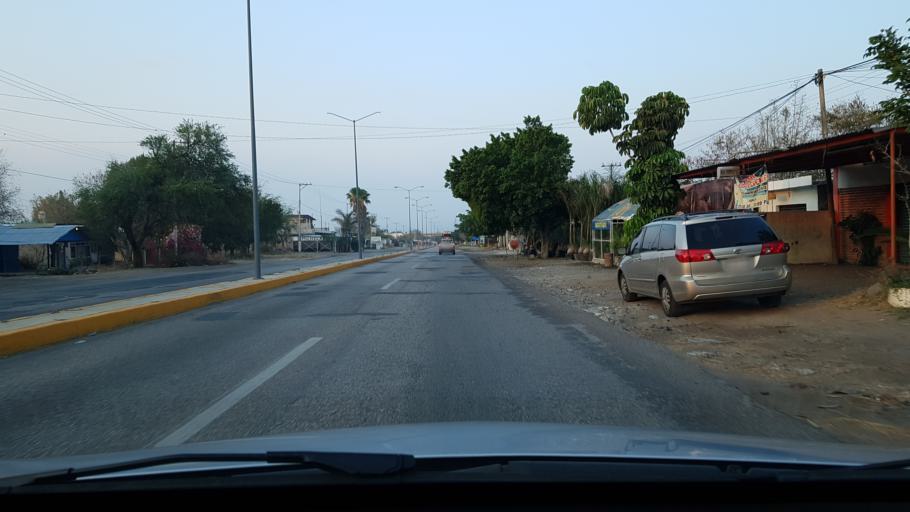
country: MX
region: Morelos
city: Amayuca
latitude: 18.7110
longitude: -98.7981
